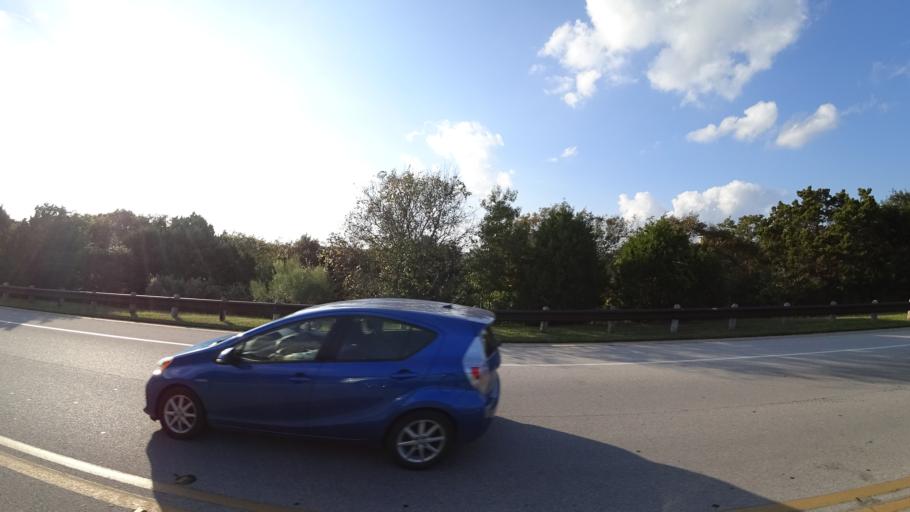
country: US
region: Texas
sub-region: Travis County
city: Lost Creek
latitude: 30.2993
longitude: -97.8469
